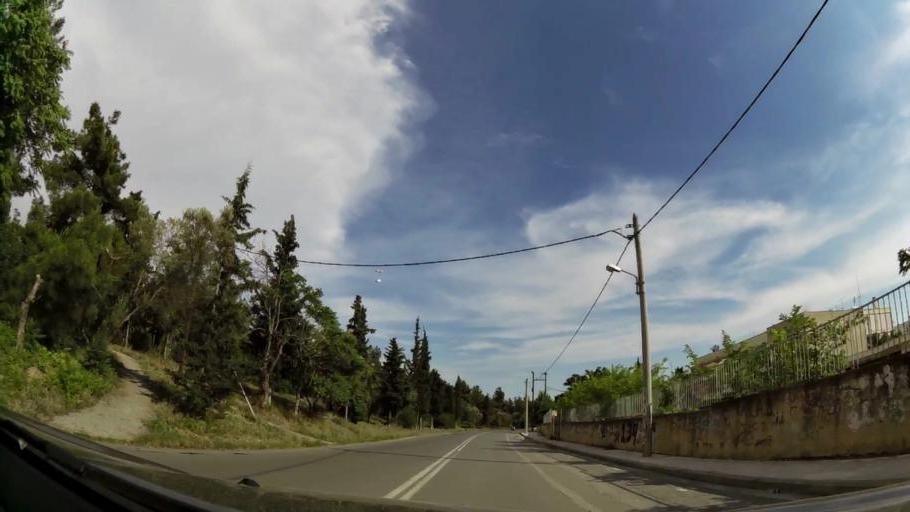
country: GR
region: Central Macedonia
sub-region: Nomos Thessalonikis
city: Kalamaria
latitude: 40.5704
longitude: 22.9753
